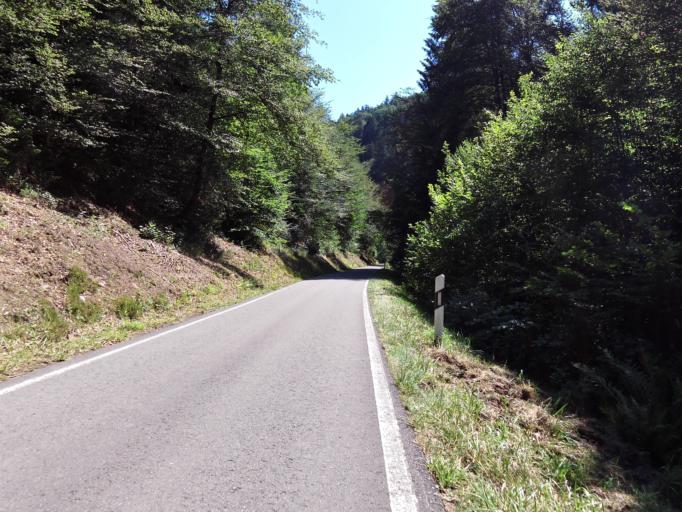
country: DE
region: Rheinland-Pfalz
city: Elmstein
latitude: 49.3690
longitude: 7.9202
